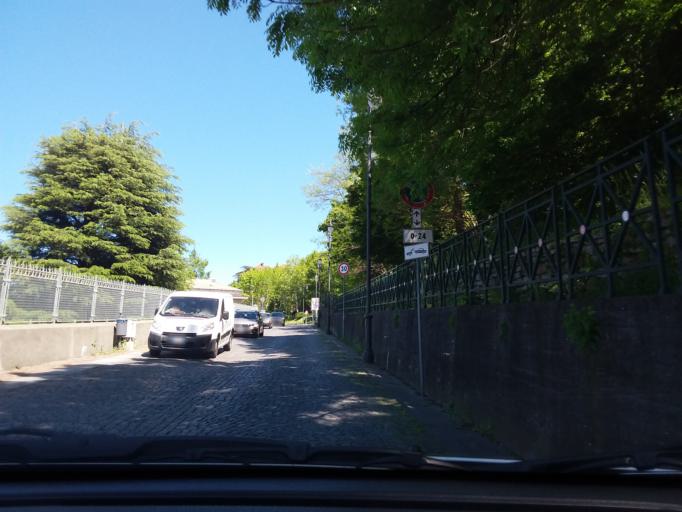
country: IT
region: Piedmont
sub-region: Provincia di Torino
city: Rivoli
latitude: 45.0697
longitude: 7.5074
